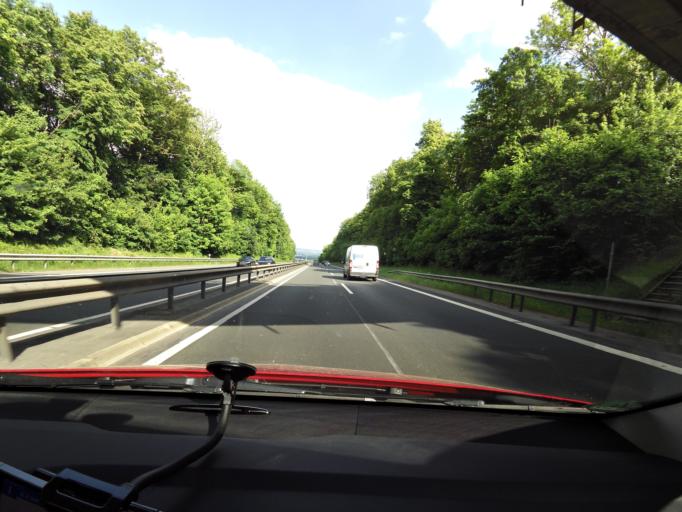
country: DE
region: Rheinland-Pfalz
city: Weissenthurm
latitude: 50.4070
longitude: 7.4551
